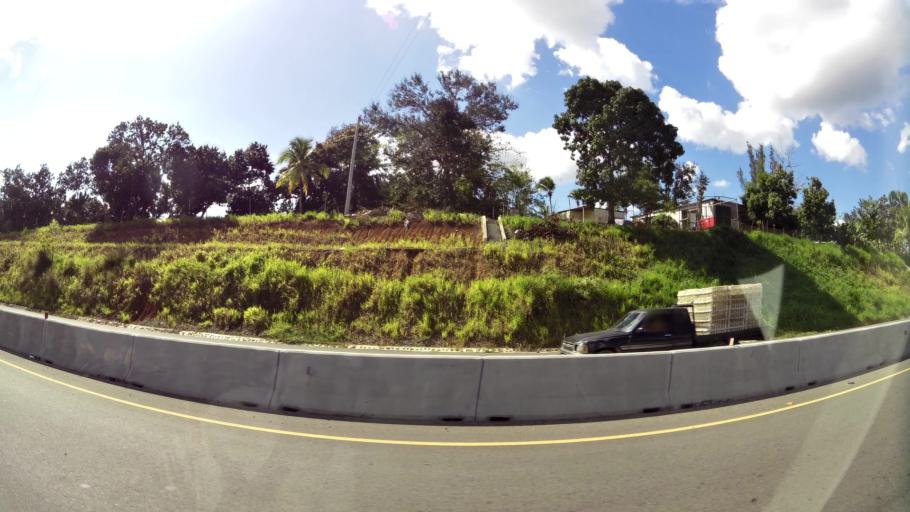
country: DO
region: Santo Domingo
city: Santo Domingo Oeste
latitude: 18.5562
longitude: -70.0713
